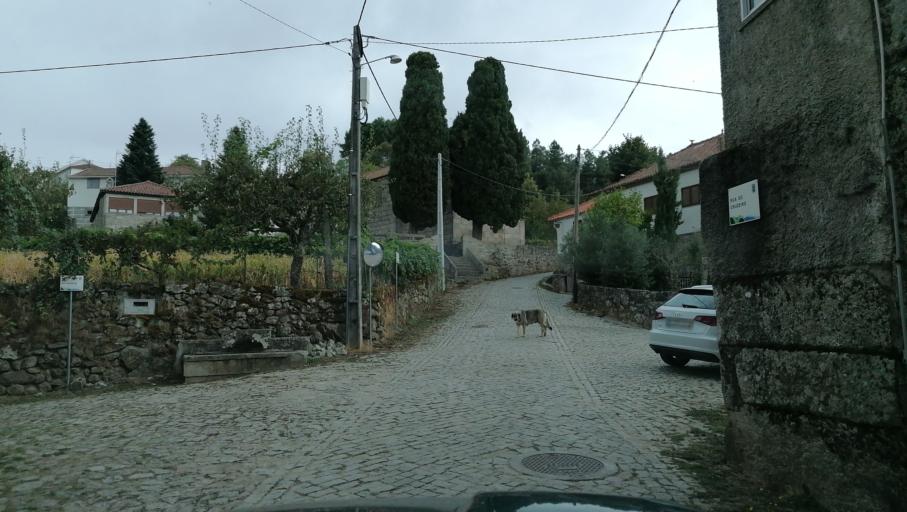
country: PT
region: Vila Real
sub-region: Vila Pouca de Aguiar
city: Vila Pouca de Aguiar
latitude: 41.5620
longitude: -7.6536
